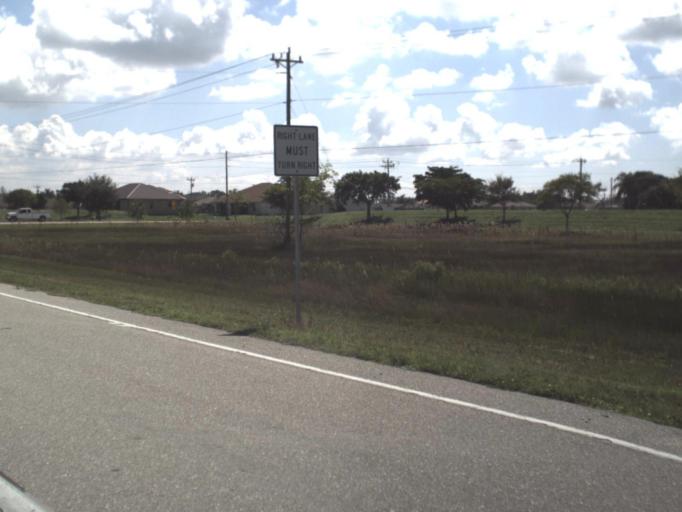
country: US
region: Florida
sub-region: Lee County
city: Cape Coral
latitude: 26.6071
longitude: -82.0206
